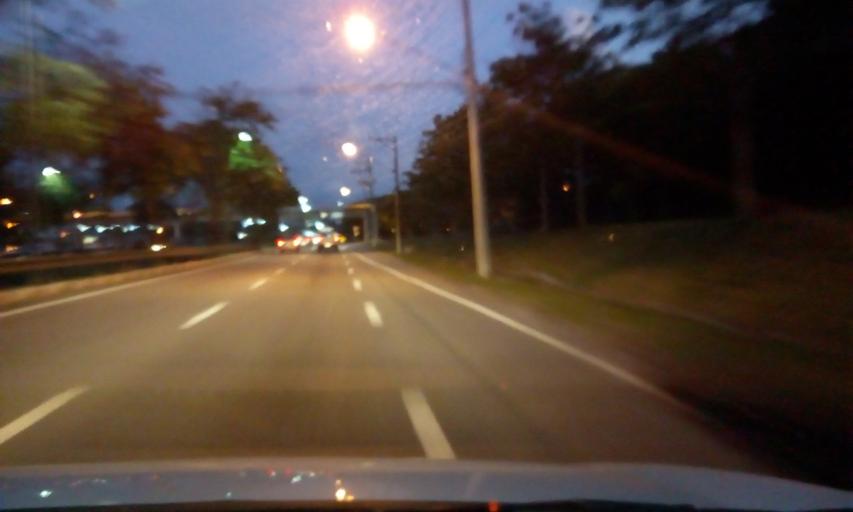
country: BR
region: Sao Paulo
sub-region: Sao Jose Dos Campos
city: Sao Jose dos Campos
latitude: -23.2153
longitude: -45.8885
